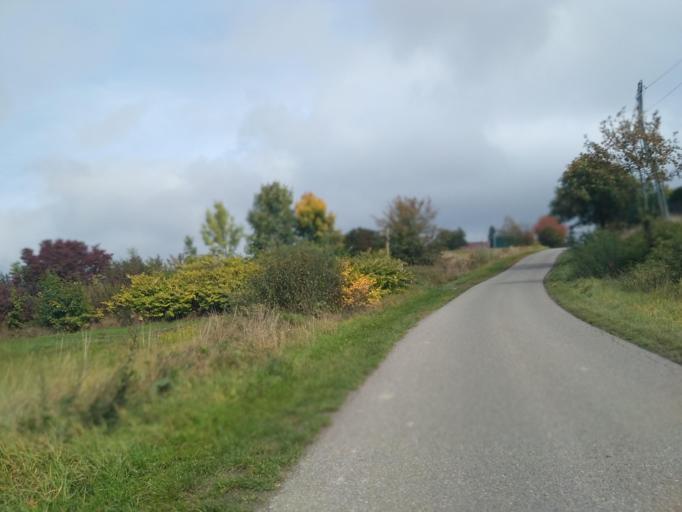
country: PL
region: Subcarpathian Voivodeship
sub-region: Powiat ropczycko-sedziszowski
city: Niedzwiada
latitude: 49.9622
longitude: 21.4431
